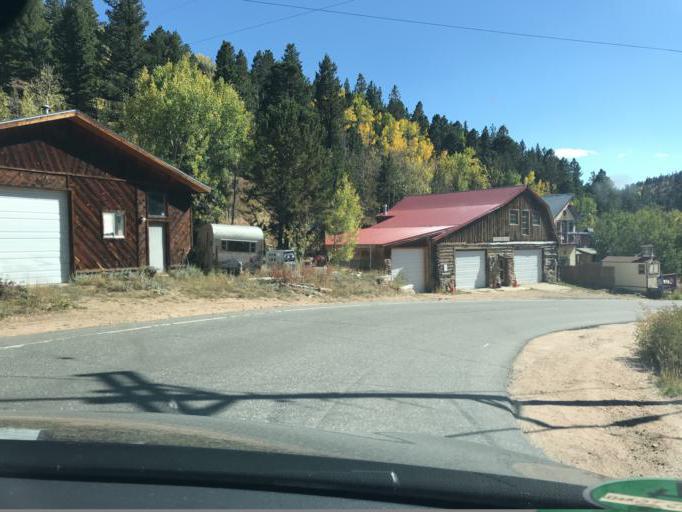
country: US
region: Colorado
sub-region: Boulder County
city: Nederland
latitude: 40.0739
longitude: -105.5063
